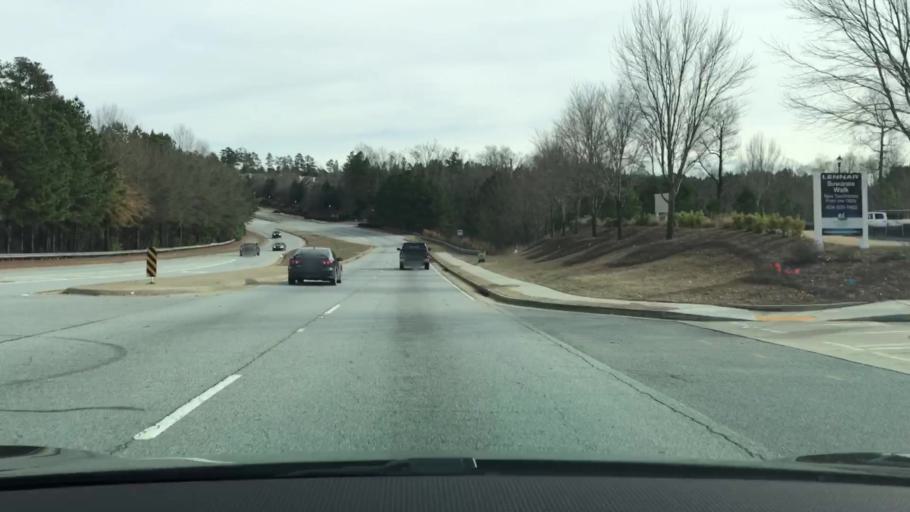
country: US
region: Georgia
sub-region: Gwinnett County
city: Suwanee
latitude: 34.0478
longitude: -84.0907
